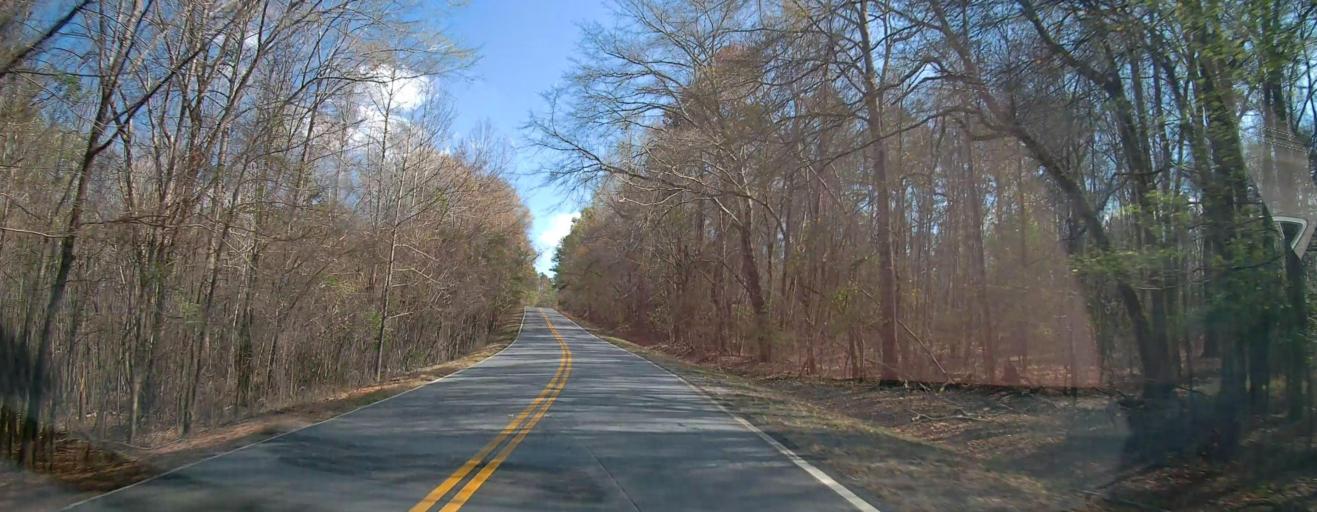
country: US
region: Georgia
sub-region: Twiggs County
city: Jeffersonville
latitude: 32.7267
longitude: -83.3491
